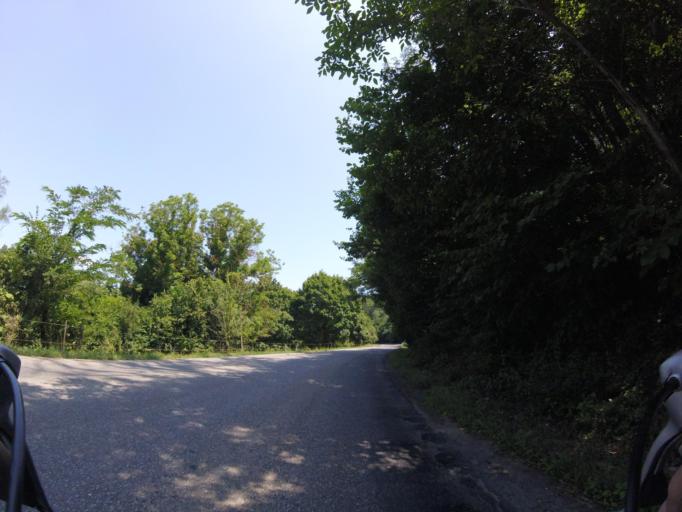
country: HU
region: Pest
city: Szob
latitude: 47.8465
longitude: 18.8482
